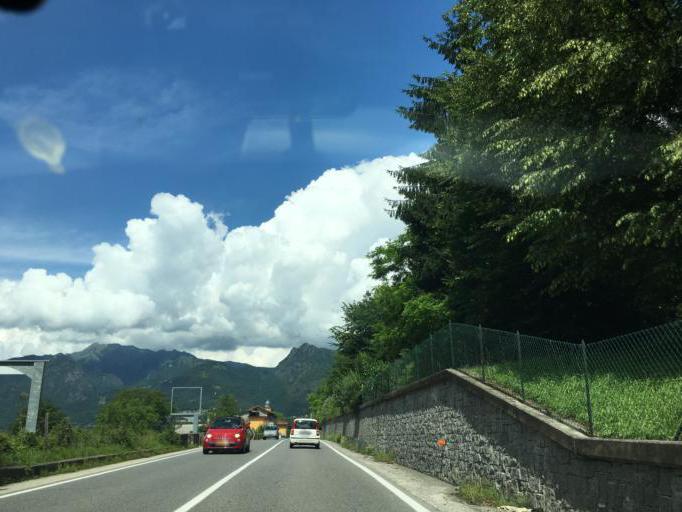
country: IT
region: Lombardy
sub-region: Provincia di Como
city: Bene Lario
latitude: 46.0317
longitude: 9.1928
